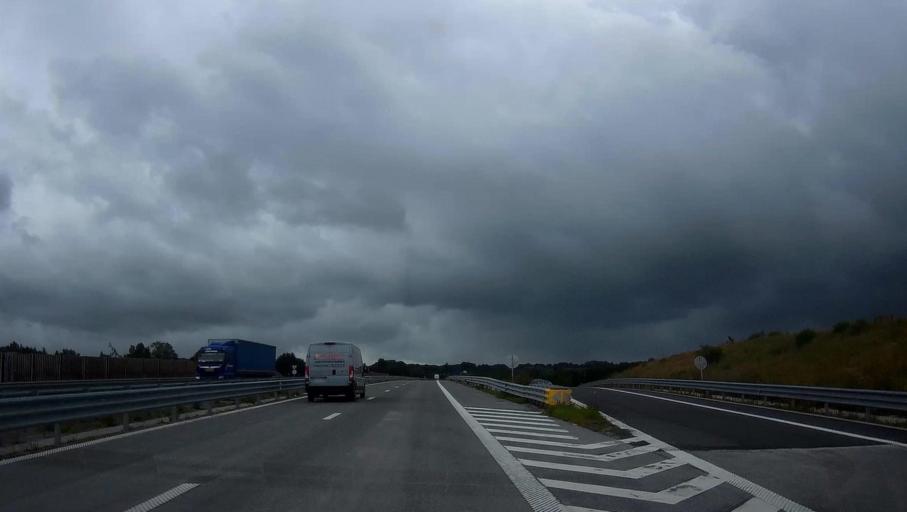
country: FR
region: Champagne-Ardenne
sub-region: Departement des Ardennes
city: Rocroi
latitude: 49.9652
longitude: 4.5355
